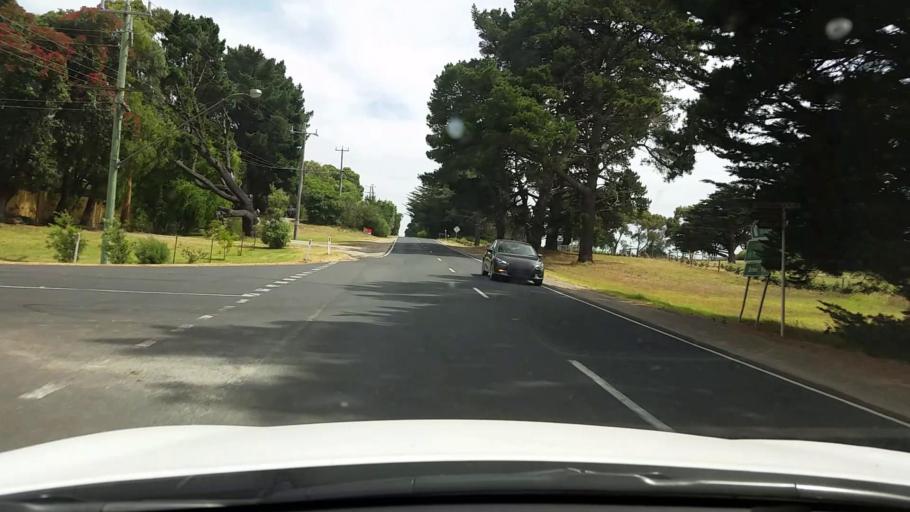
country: AU
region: Victoria
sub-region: Mornington Peninsula
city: Saint Andrews Beach
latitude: -38.4599
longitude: 144.9043
